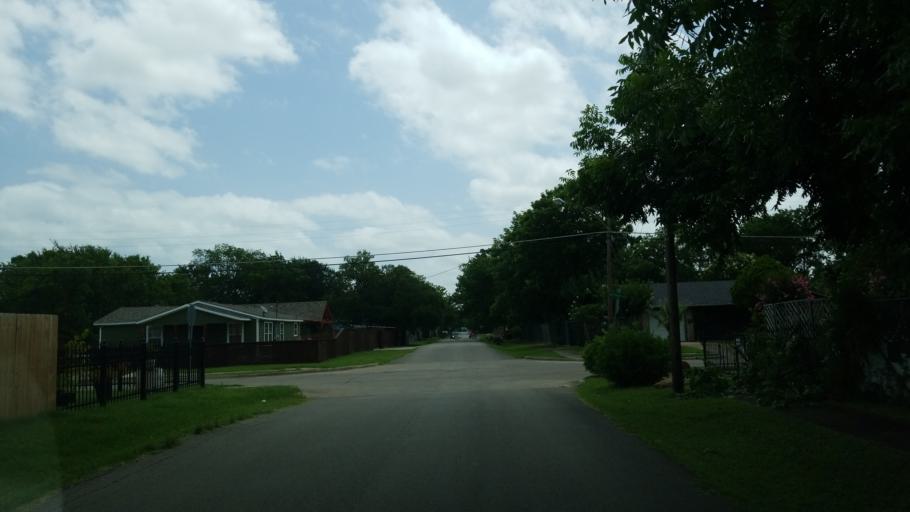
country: US
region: Texas
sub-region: Dallas County
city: Irving
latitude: 32.7871
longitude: -96.9050
